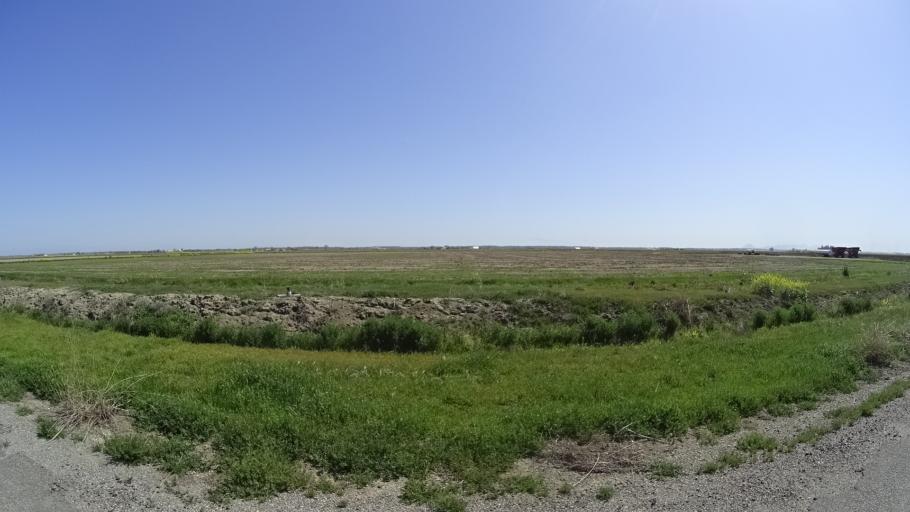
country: US
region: California
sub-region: Glenn County
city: Willows
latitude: 39.4369
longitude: -122.0647
